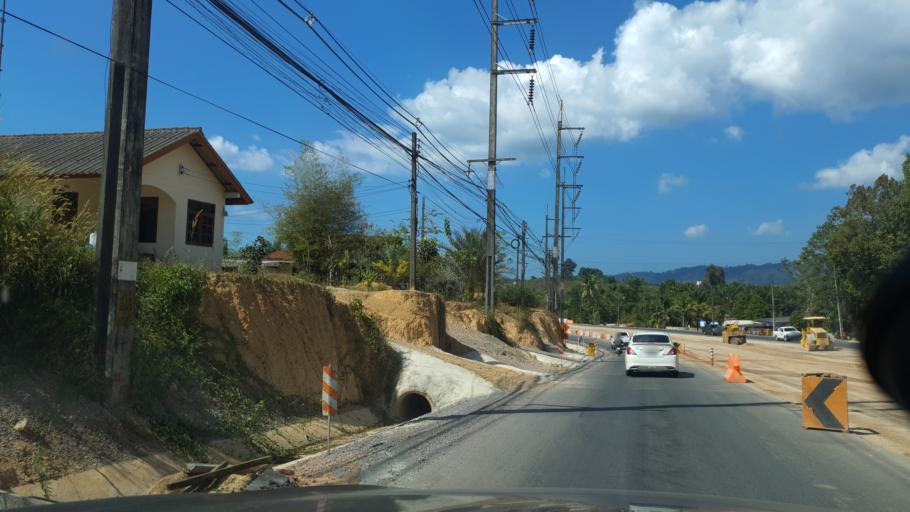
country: TH
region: Phangnga
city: Ban Khao Lak
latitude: 8.5591
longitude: 98.2698
